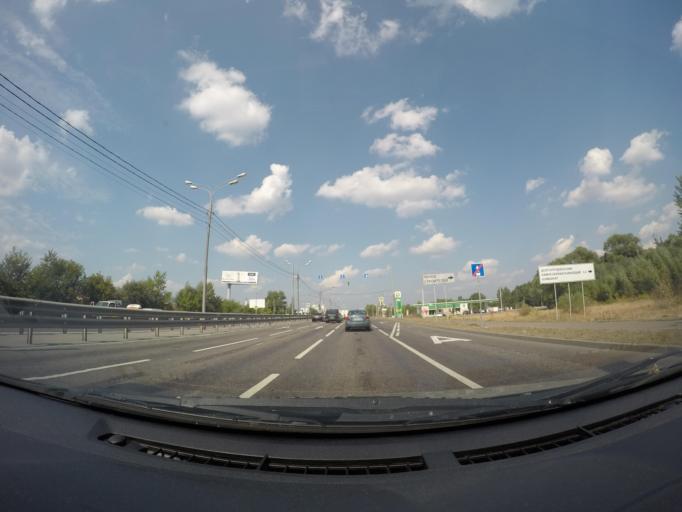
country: RU
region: Moscow
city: Businovo
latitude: 55.9116
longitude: 37.4946
